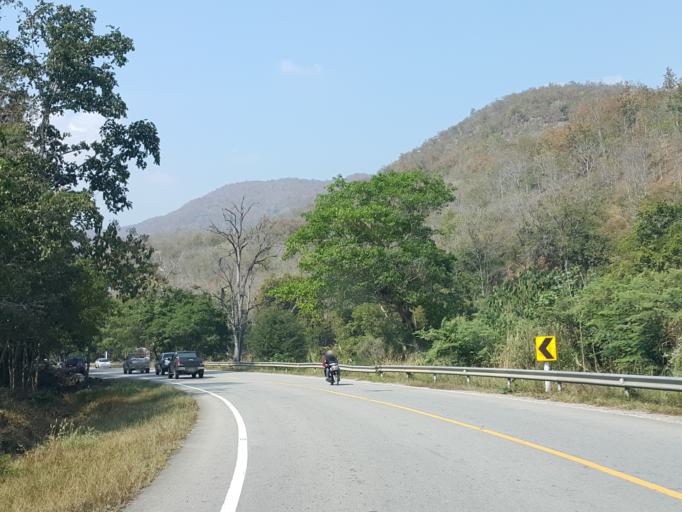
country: TH
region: Chiang Mai
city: Hot
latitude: 18.2337
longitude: 98.5485
